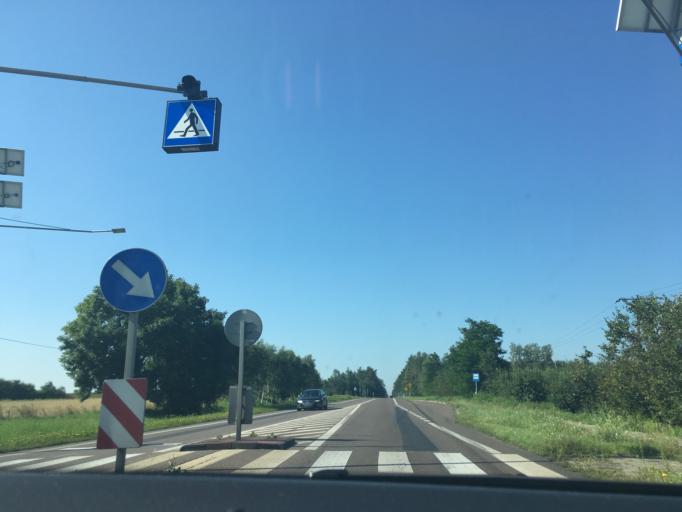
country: PL
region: Lublin Voivodeship
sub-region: Powiat radzynski
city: Radzyn Podlaski
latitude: 51.7652
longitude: 22.5774
